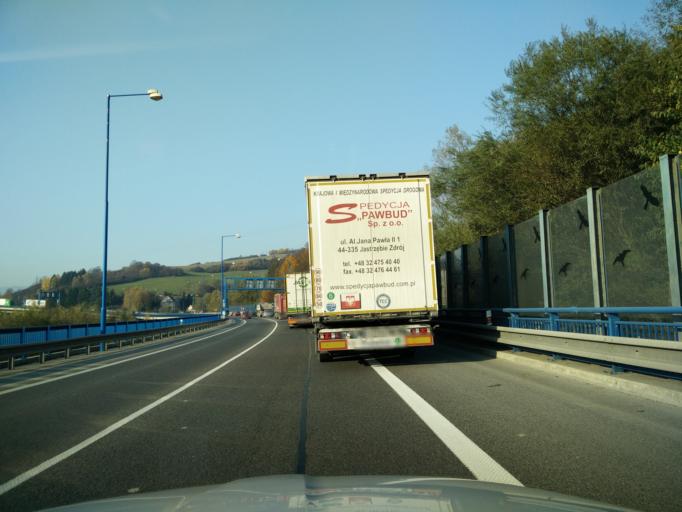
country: SK
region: Zilinsky
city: Cadca
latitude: 49.4372
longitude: 18.7992
